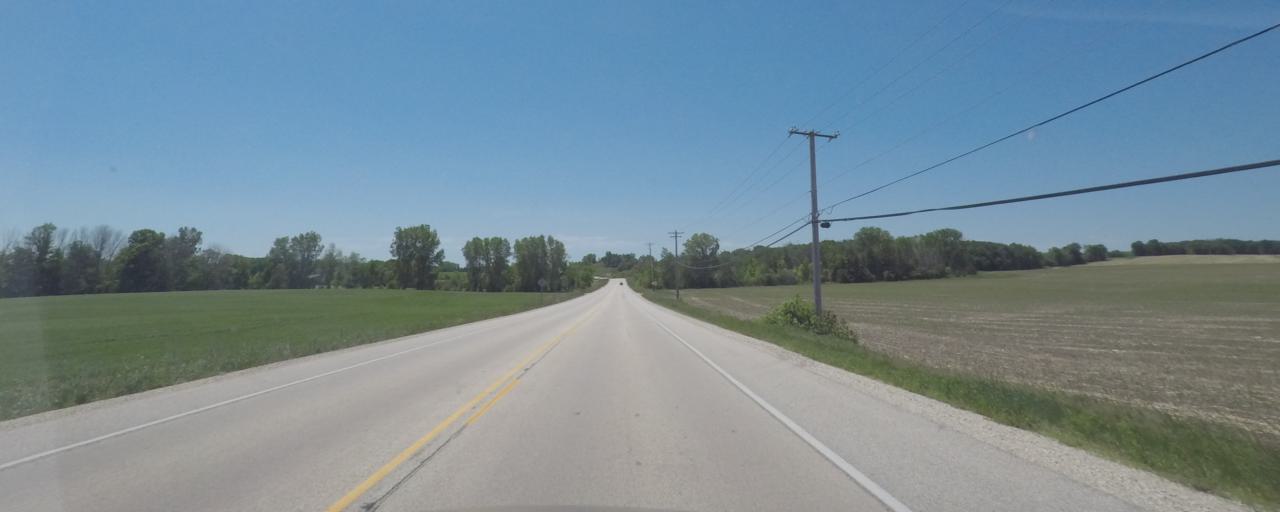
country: US
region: Wisconsin
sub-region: Washington County
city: West Bend
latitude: 43.4643
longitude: -88.1538
